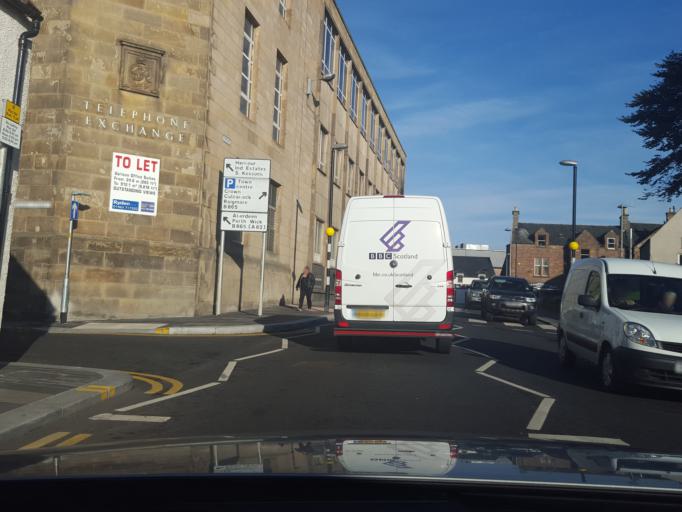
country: GB
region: Scotland
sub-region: Highland
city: Inverness
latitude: 57.4801
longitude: -4.2295
